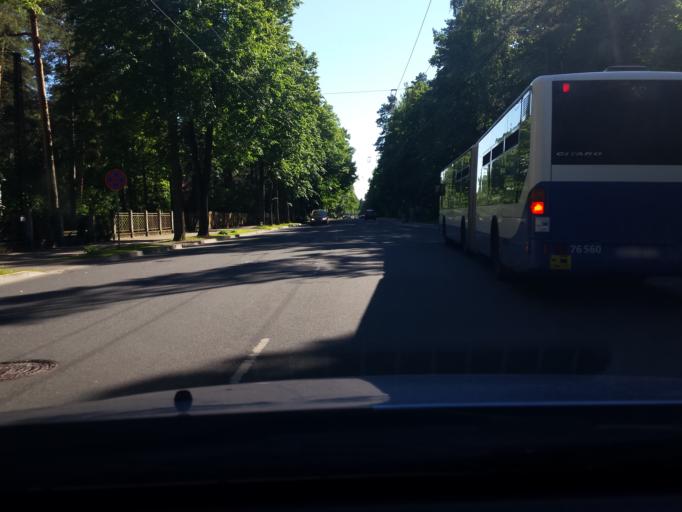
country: LV
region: Riga
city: Jaunciems
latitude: 57.0024
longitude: 24.1520
